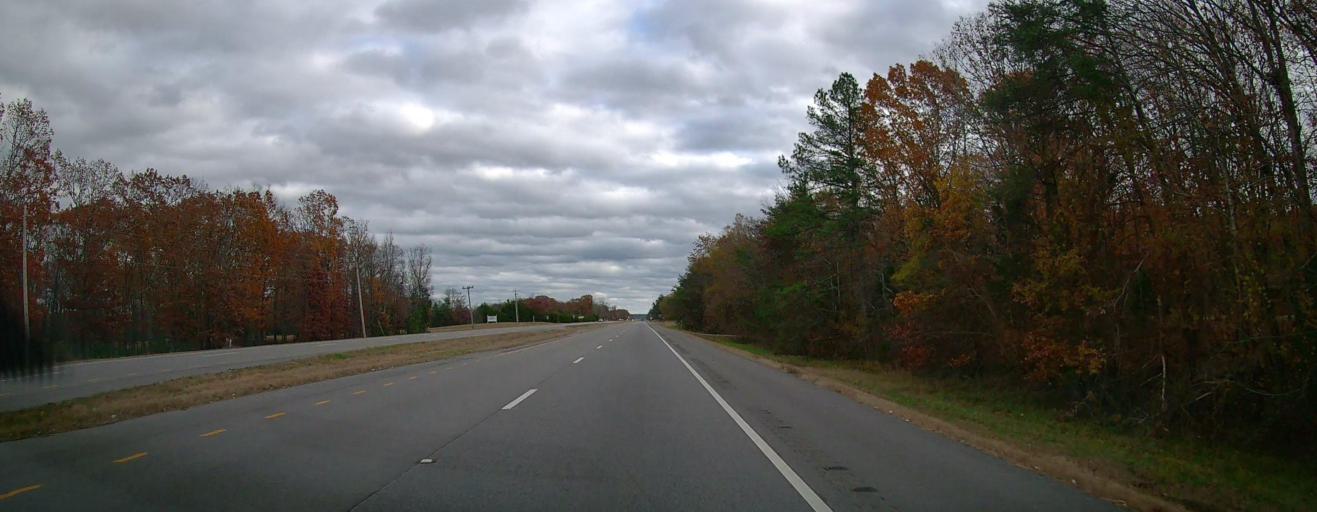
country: US
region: Alabama
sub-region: Colbert County
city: Muscle Shoals
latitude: 34.6662
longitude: -87.5536
